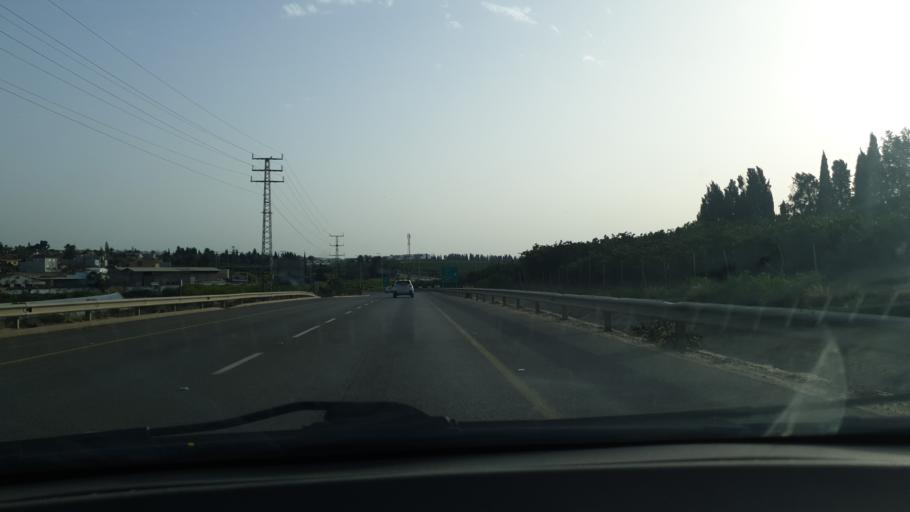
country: IL
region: Central District
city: Tel Mond
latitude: 32.2646
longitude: 34.9170
